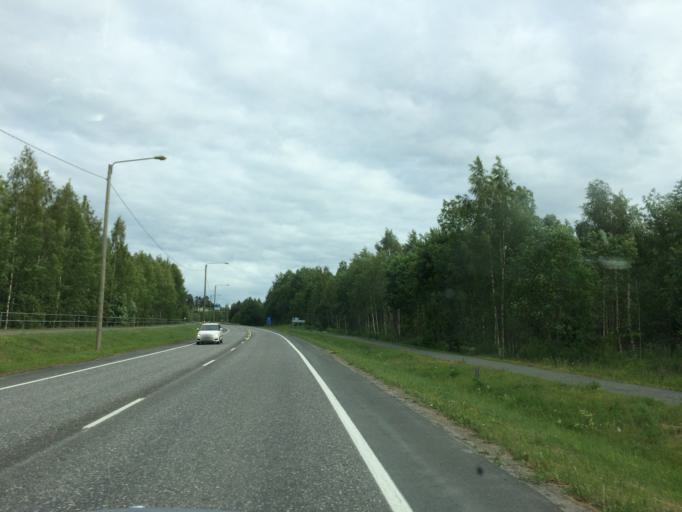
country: FI
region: Haeme
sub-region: Haemeenlinna
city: Haemeenlinna
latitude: 60.9690
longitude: 24.4779
